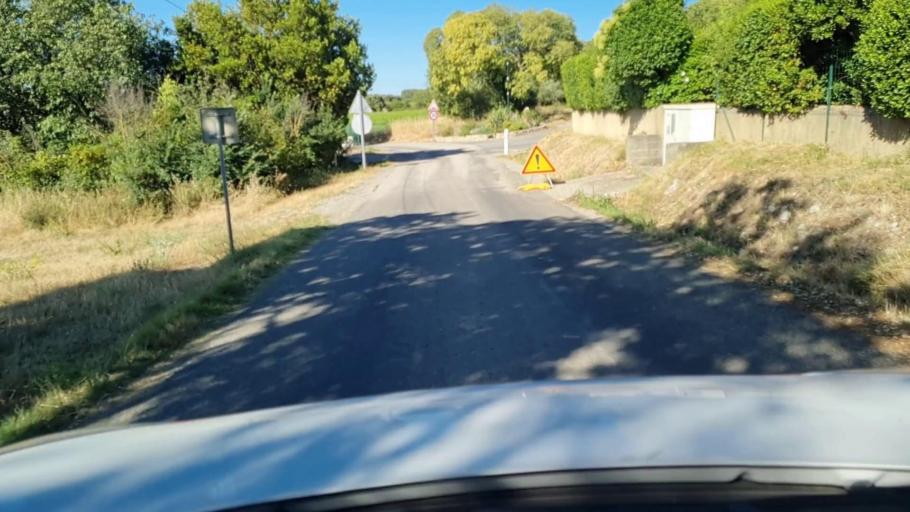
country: FR
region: Languedoc-Roussillon
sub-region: Departement du Gard
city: Sommieres
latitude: 43.8053
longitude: 4.0404
